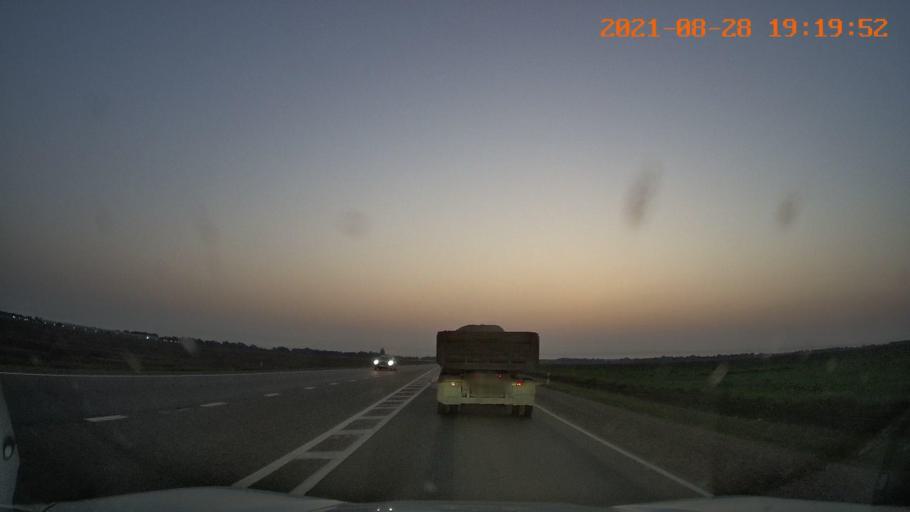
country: RU
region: Krasnodarskiy
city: Ryazanskaya
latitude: 44.8906
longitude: 39.5099
